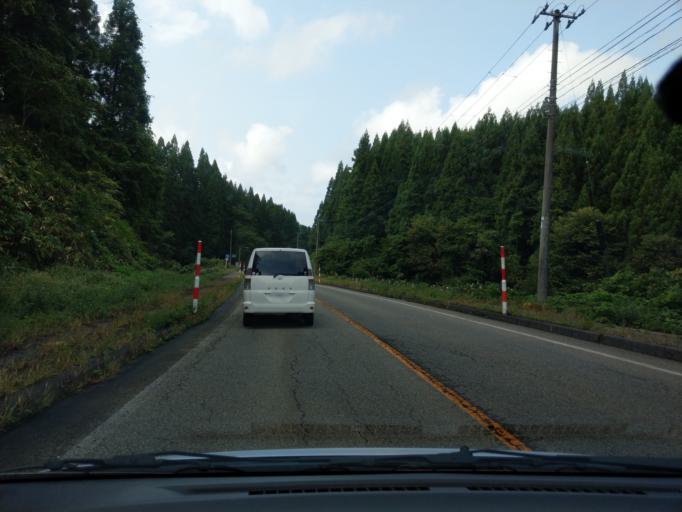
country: JP
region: Akita
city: Omagari
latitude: 39.4347
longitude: 140.3740
